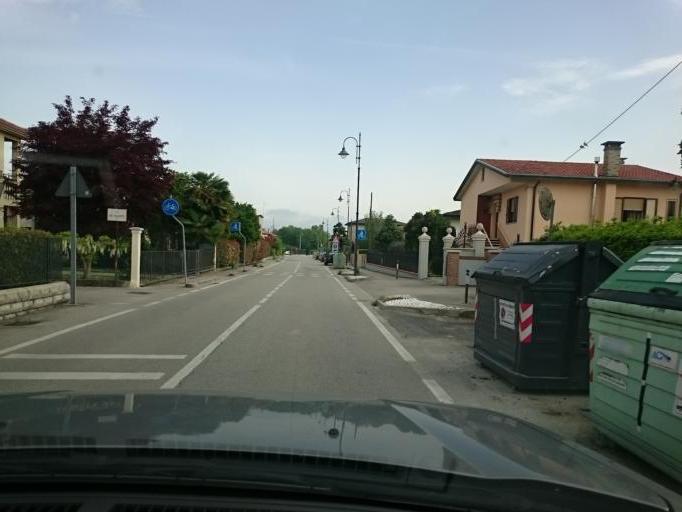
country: IT
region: Veneto
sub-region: Provincia di Venezia
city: Fornase
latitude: 45.4432
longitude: 12.1586
